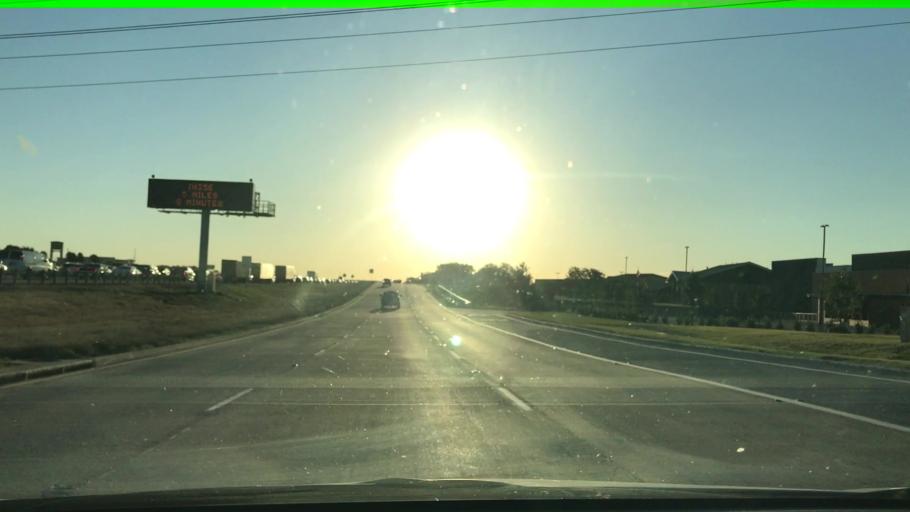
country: US
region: Texas
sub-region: Dallas County
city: Coppell
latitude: 32.9207
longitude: -96.9841
